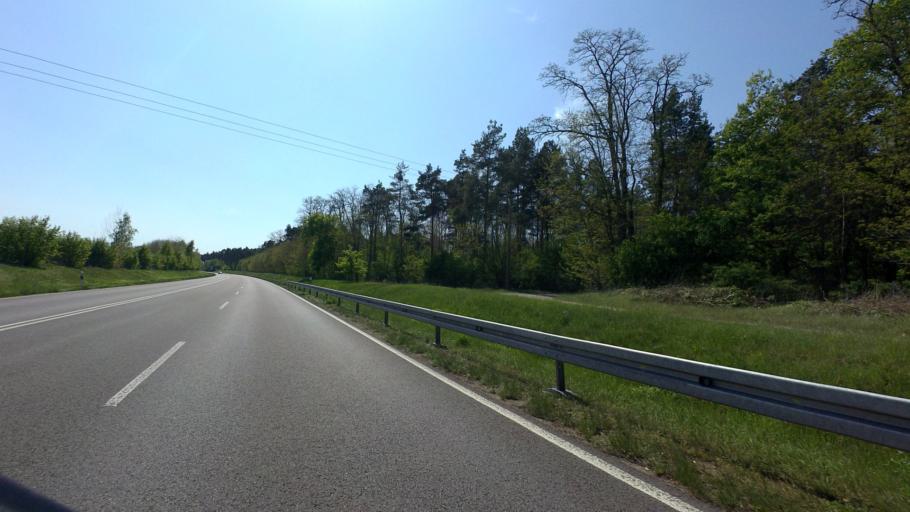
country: DE
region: Brandenburg
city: Beeskow
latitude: 52.1922
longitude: 14.2225
